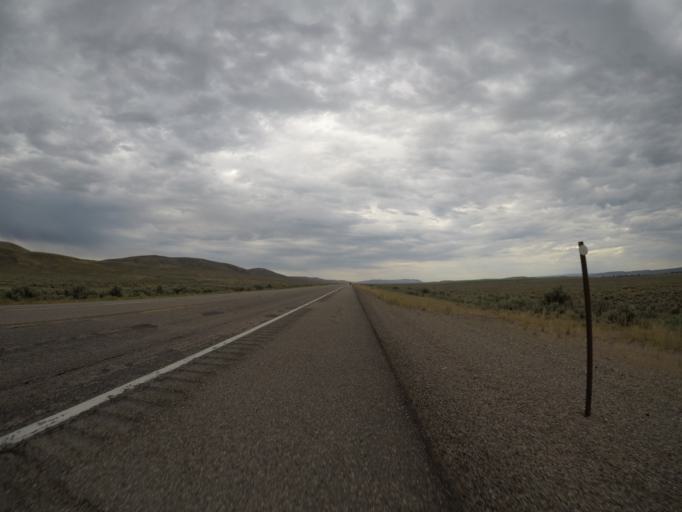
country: US
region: Utah
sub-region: Rich County
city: Randolph
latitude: 41.8807
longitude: -110.9646
